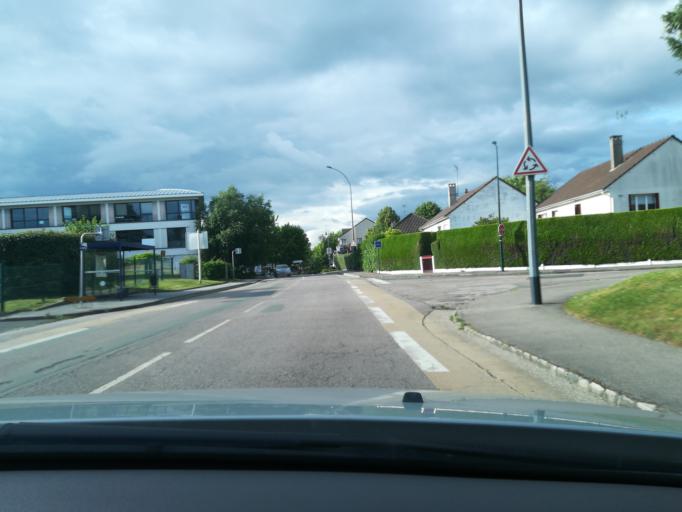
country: FR
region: Haute-Normandie
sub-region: Departement de la Seine-Maritime
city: Bois-Guillaume
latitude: 49.4780
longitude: 1.1131
